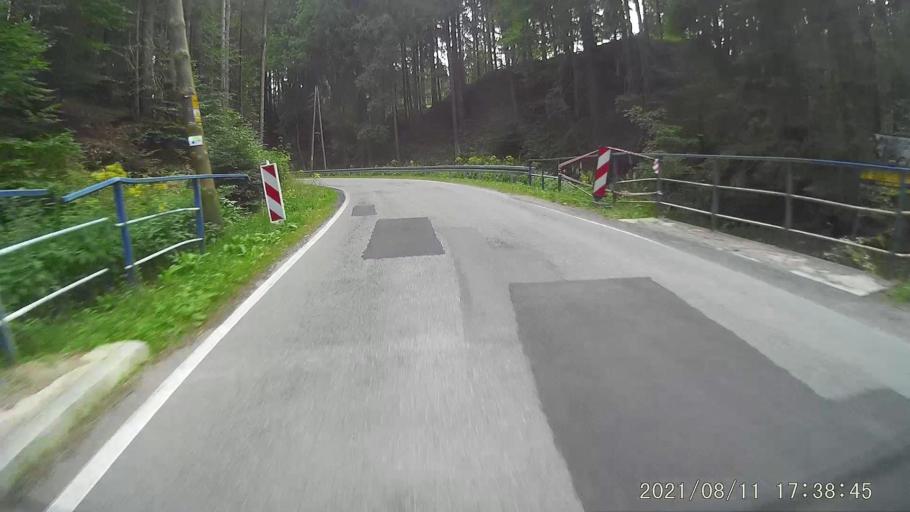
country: PL
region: Lower Silesian Voivodeship
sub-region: Powiat klodzki
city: Duszniki-Zdroj
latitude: 50.3460
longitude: 16.4007
